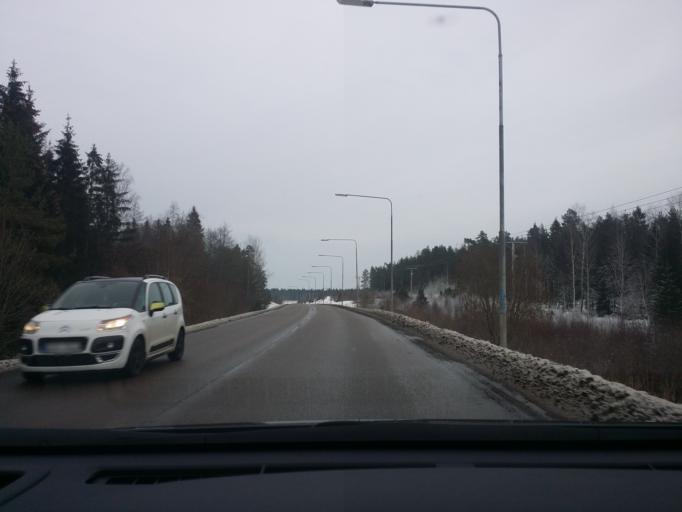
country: SE
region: Vaestra Goetaland
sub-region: Mariestads Kommun
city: Mariestad
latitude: 58.6938
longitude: 13.8476
